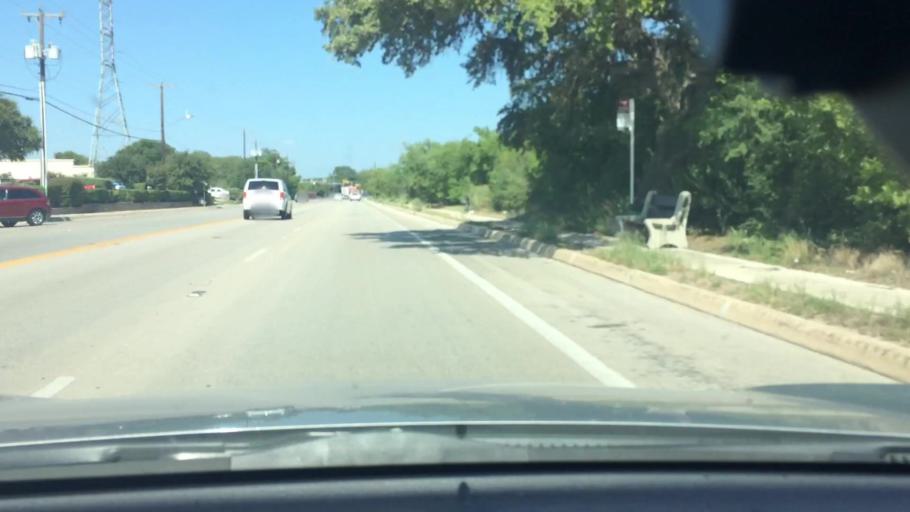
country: US
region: Texas
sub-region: Bexar County
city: China Grove
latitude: 29.3745
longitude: -98.4011
